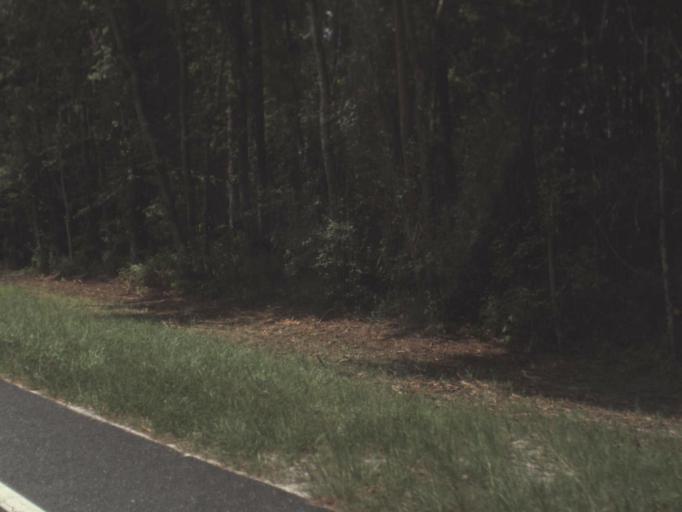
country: US
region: Georgia
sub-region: Echols County
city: Statenville
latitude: 30.6213
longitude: -83.1176
